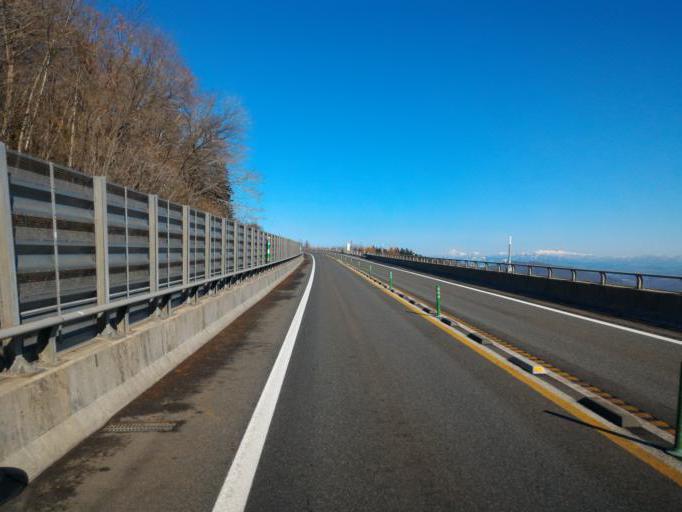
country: JP
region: Hokkaido
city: Otofuke
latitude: 43.0466
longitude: 142.7839
